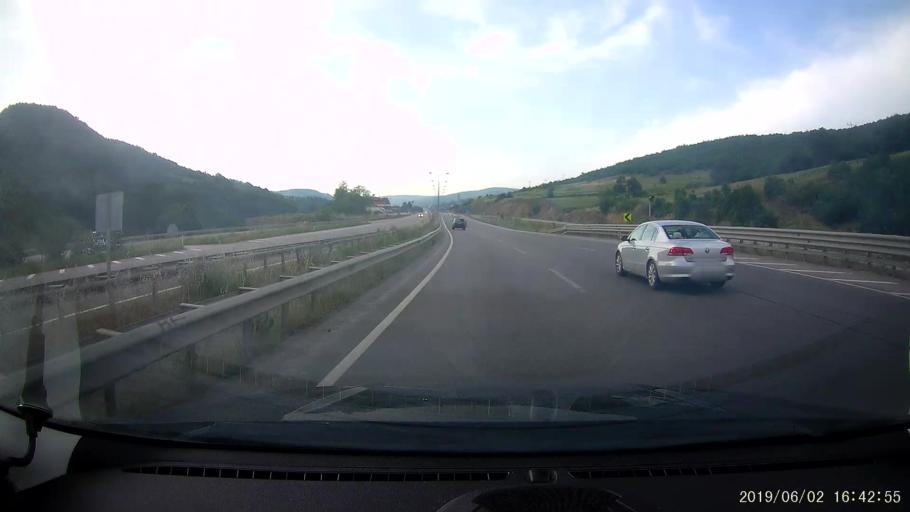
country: TR
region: Samsun
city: Kavak
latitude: 41.1265
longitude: 36.1375
